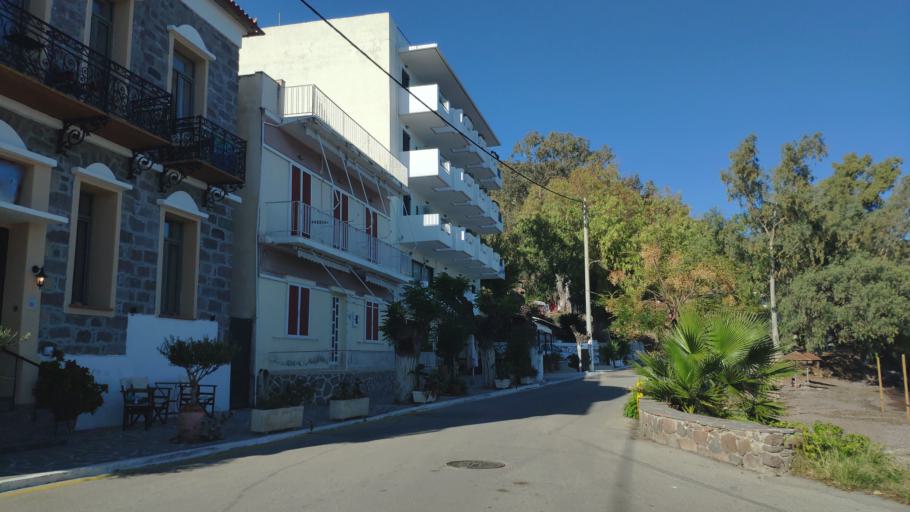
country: GR
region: Attica
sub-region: Nomos Piraios
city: Poros
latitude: 37.5838
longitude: 23.3938
